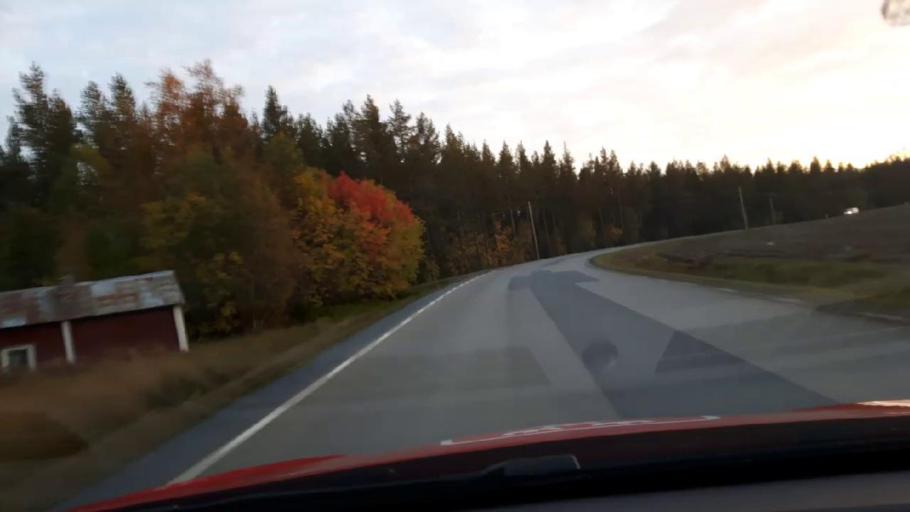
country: SE
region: Jaemtland
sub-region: OEstersunds Kommun
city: Ostersund
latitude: 63.2495
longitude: 14.6002
